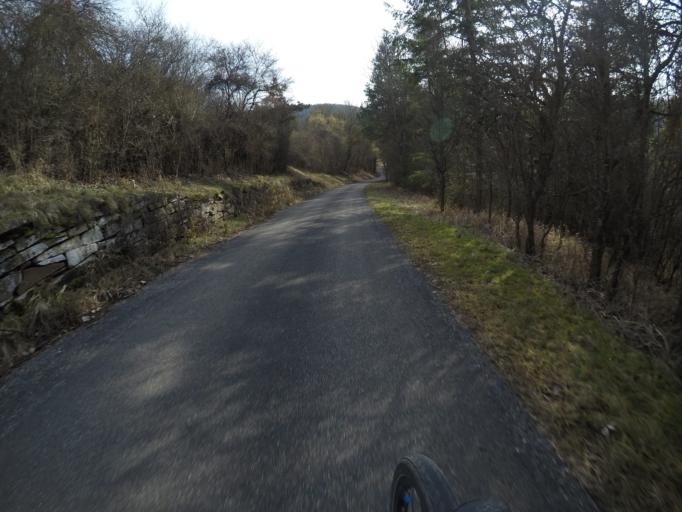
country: DE
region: Baden-Wuerttemberg
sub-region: Karlsruhe Region
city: Wildberg
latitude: 48.6328
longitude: 8.7686
